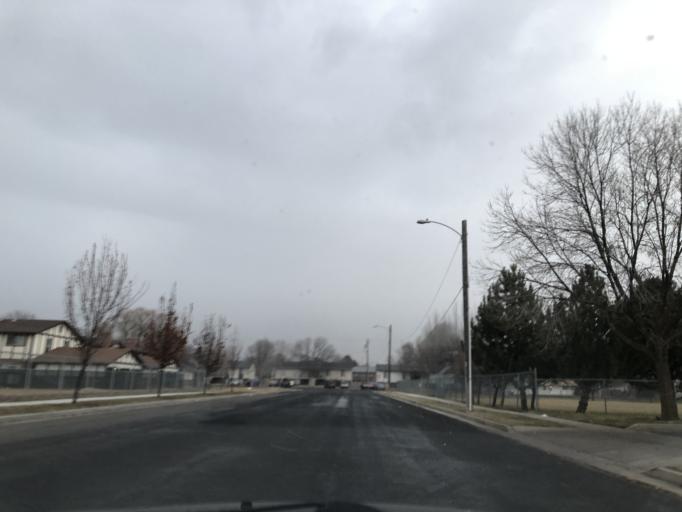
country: US
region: Utah
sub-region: Cache County
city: Logan
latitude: 41.7187
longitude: -111.8440
